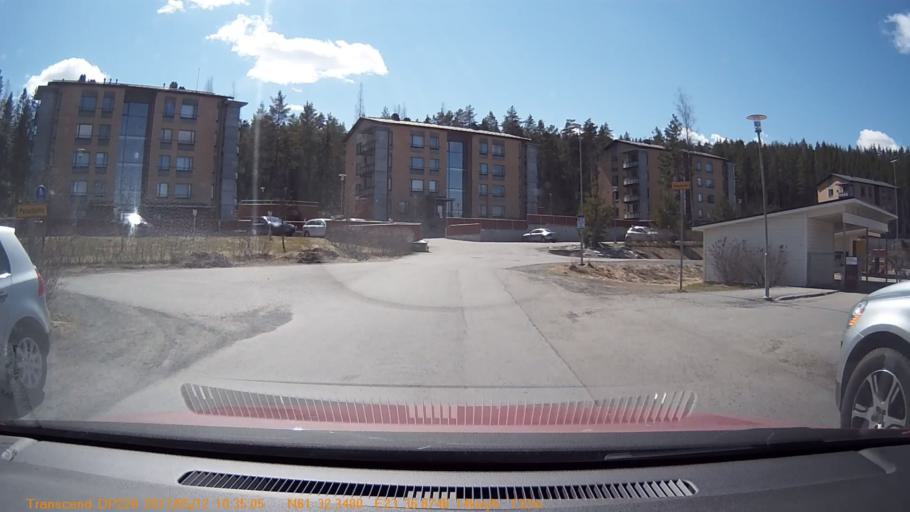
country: FI
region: Pirkanmaa
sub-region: Tampere
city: Yloejaervi
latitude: 61.5392
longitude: 23.6147
